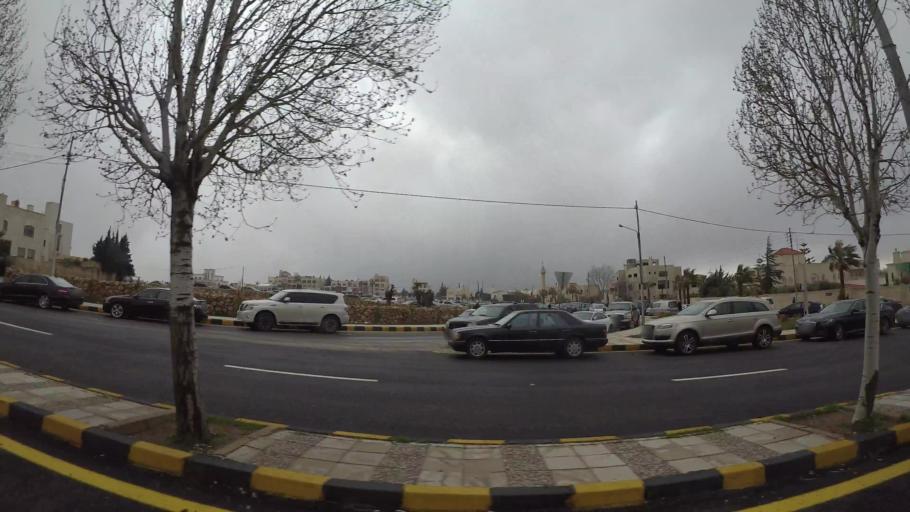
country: JO
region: Amman
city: Al Bunayyat ash Shamaliyah
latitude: 31.9396
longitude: 35.8793
